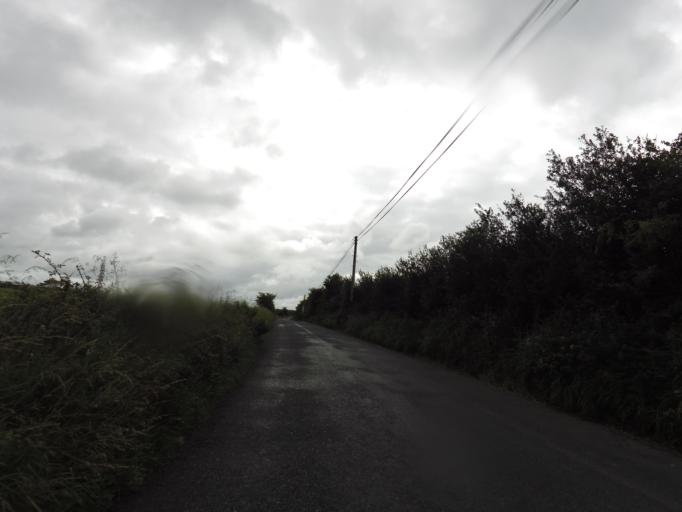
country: IE
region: Connaught
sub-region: County Galway
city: Athenry
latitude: 53.2911
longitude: -8.7011
